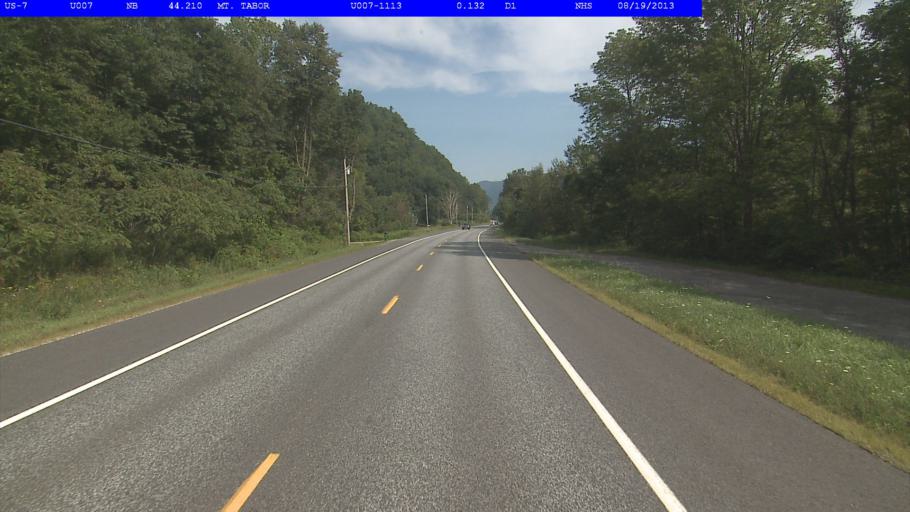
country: US
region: Vermont
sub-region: Bennington County
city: Manchester Center
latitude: 43.3069
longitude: -72.9946
